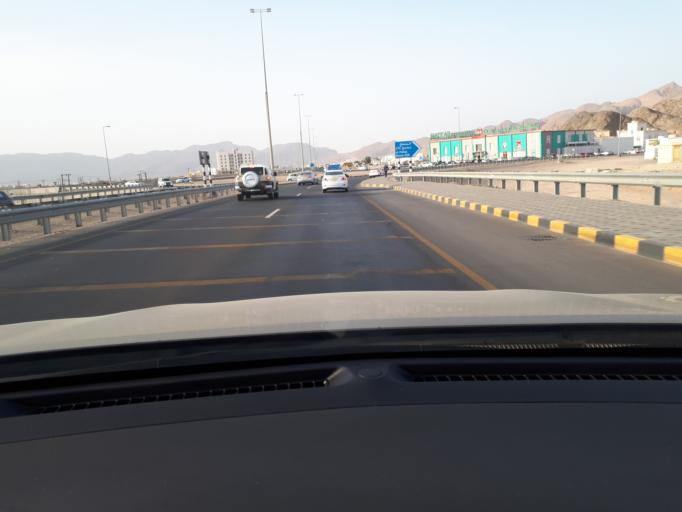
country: OM
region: Muhafazat Masqat
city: Bawshar
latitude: 23.4785
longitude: 58.4972
